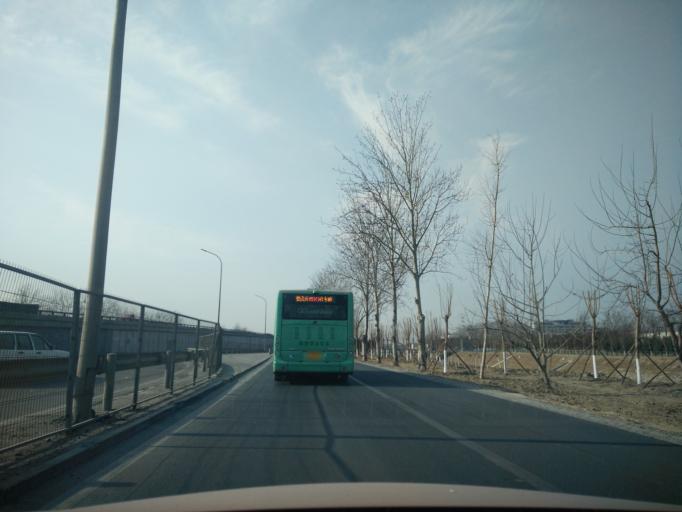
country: CN
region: Beijing
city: Yinghai
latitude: 39.7200
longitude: 116.4060
